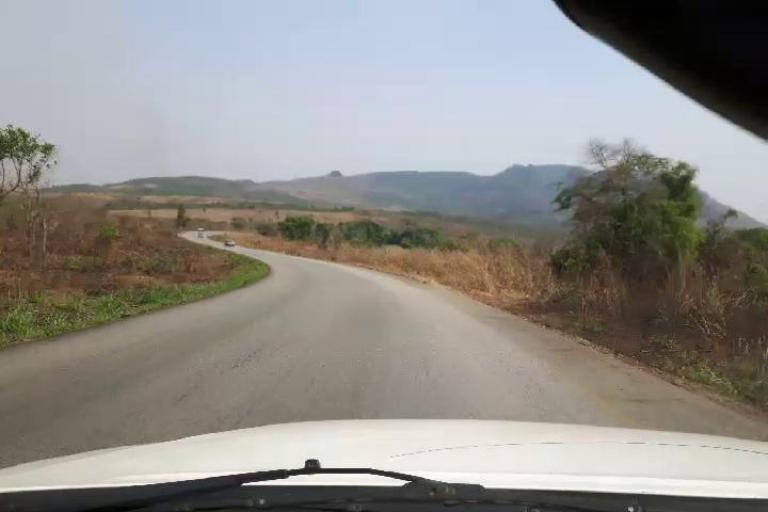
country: SL
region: Northern Province
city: Yonibana
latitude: 8.3860
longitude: -12.1927
